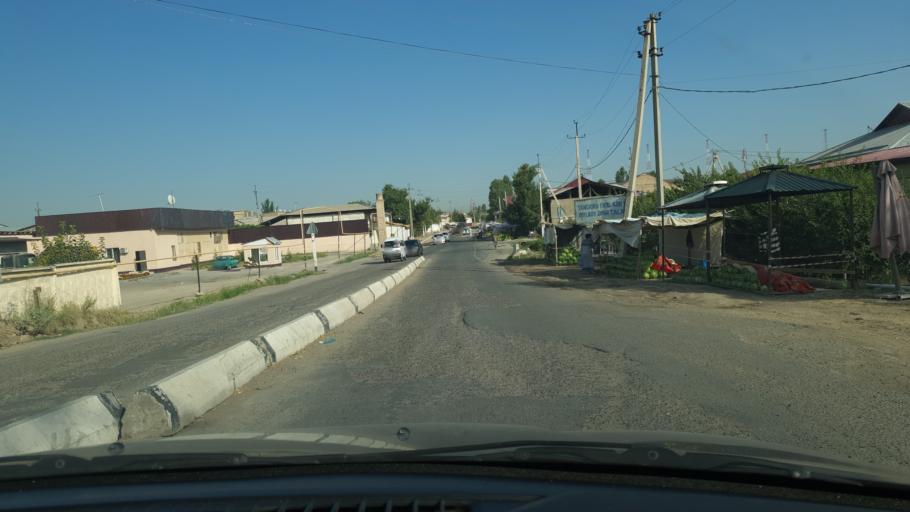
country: UZ
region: Toshkent
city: Urtaowul
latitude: 41.2013
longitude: 69.1553
